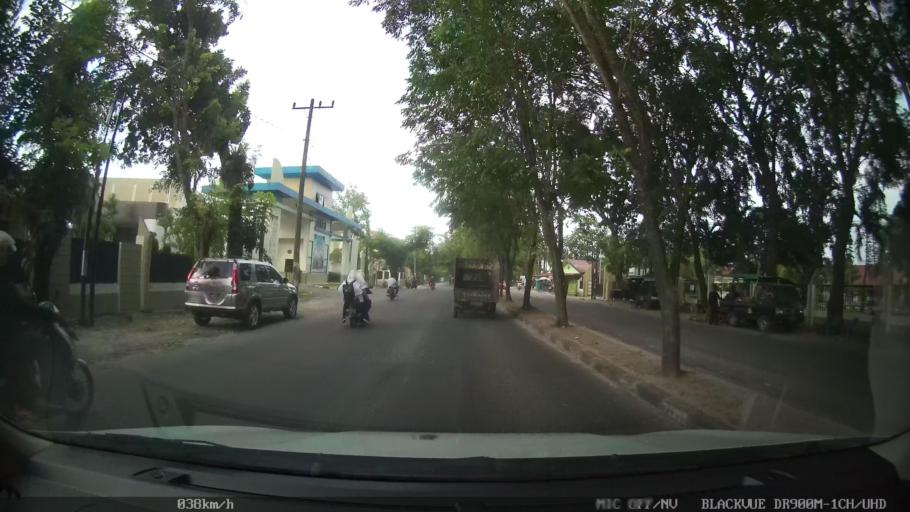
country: ID
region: North Sumatra
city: Sunggal
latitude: 3.5538
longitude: 98.6125
